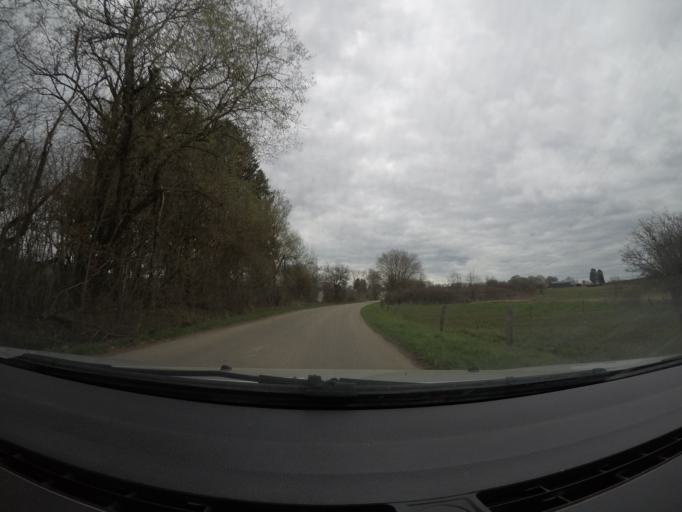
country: BE
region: Wallonia
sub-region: Province du Luxembourg
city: Leglise
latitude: 49.7814
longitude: 5.5963
